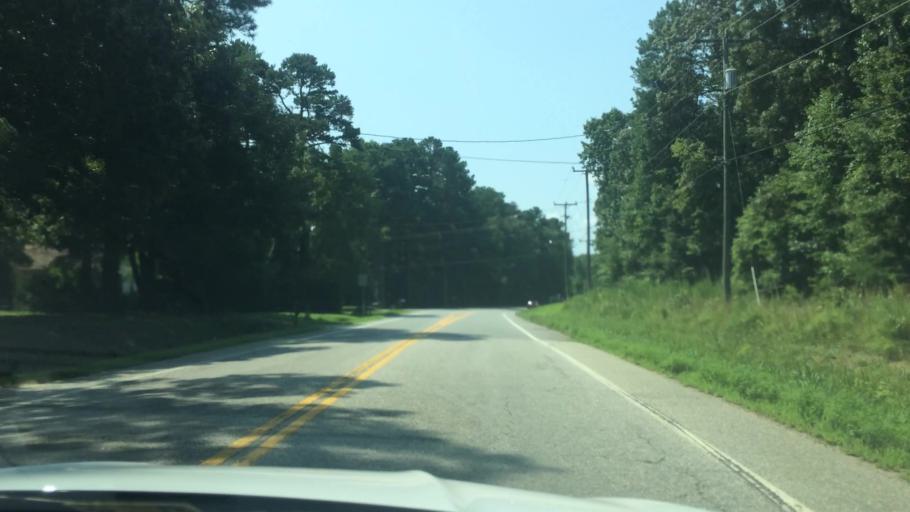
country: US
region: Virginia
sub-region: James City County
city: Williamsburg
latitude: 37.3188
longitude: -76.7887
